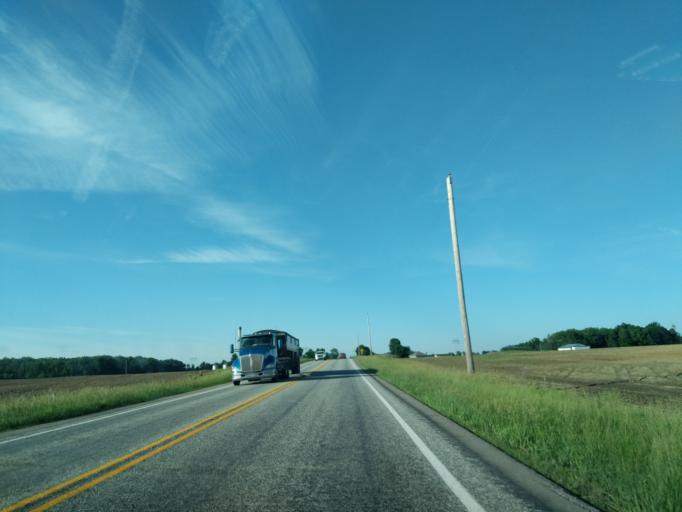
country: US
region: Indiana
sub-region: Madison County
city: Ingalls
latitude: 39.9486
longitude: -85.7660
